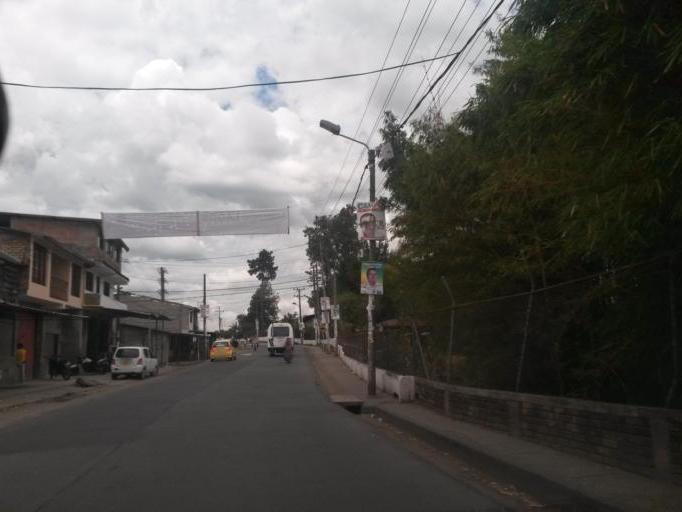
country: CO
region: Cauca
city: Popayan
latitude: 2.4498
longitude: -76.6309
